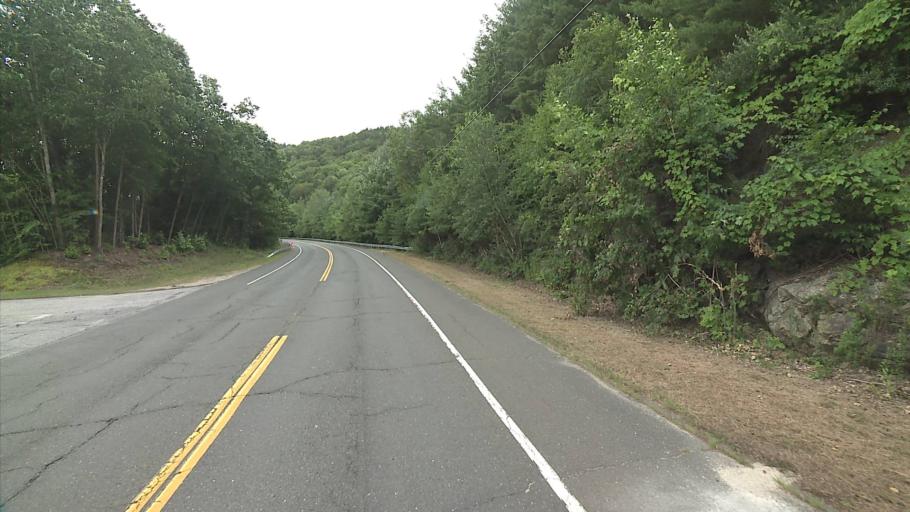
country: US
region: Connecticut
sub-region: Litchfield County
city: Winsted
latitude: 42.0192
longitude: -73.0529
